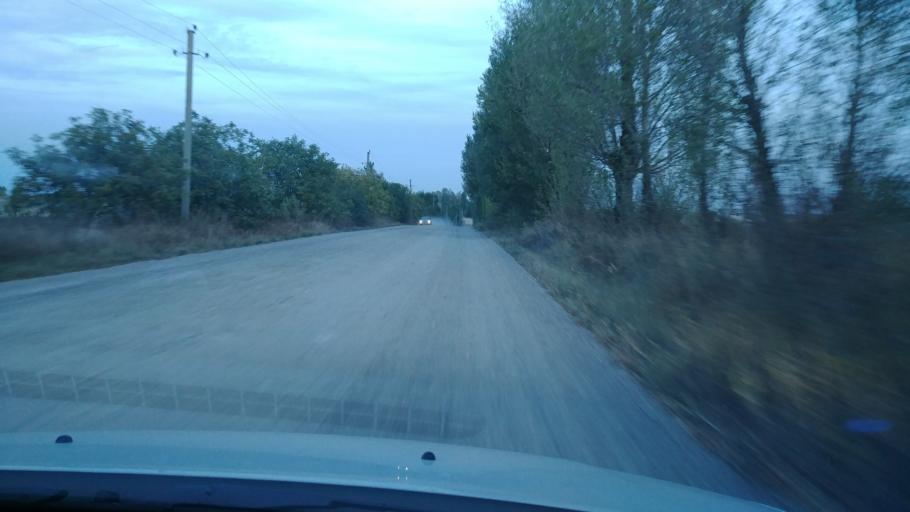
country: MD
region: Rezina
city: Saharna
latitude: 47.6789
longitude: 28.9207
